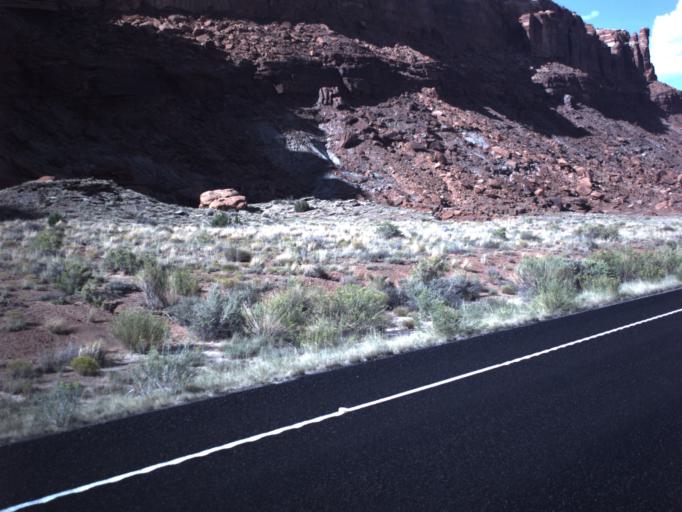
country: US
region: Utah
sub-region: Grand County
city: Moab
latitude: 38.6592
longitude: -109.7080
